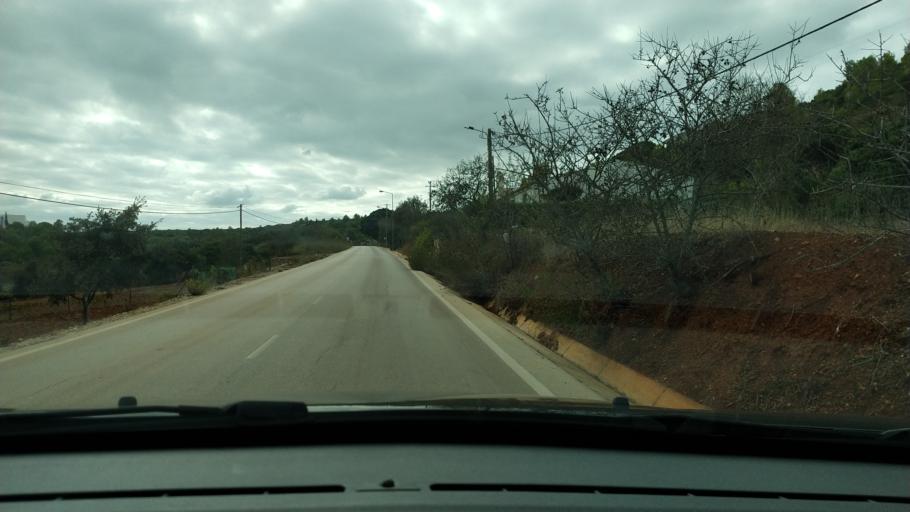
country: PT
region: Faro
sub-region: Vila do Bispo
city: Vila do Bispo
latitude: 37.0701
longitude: -8.7957
